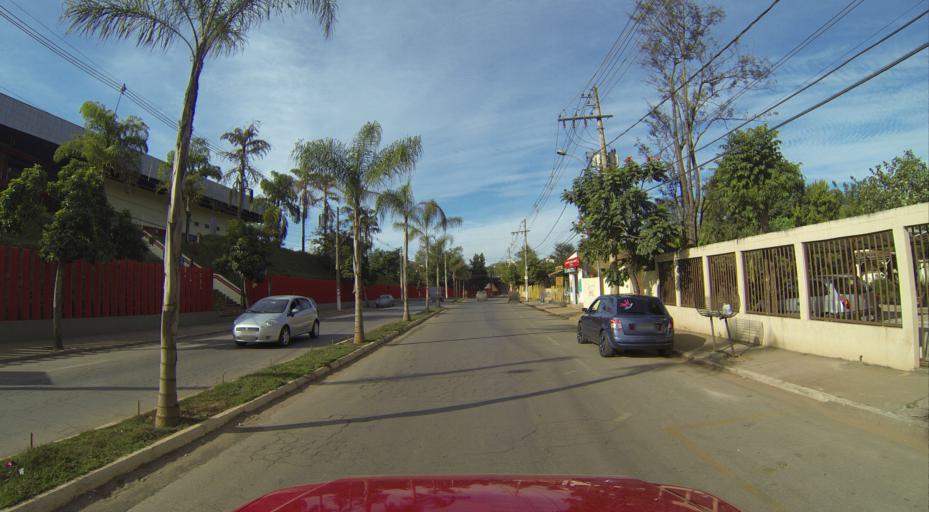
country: BR
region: Minas Gerais
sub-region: Brumadinho
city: Brumadinho
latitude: -20.1432
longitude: -44.2117
